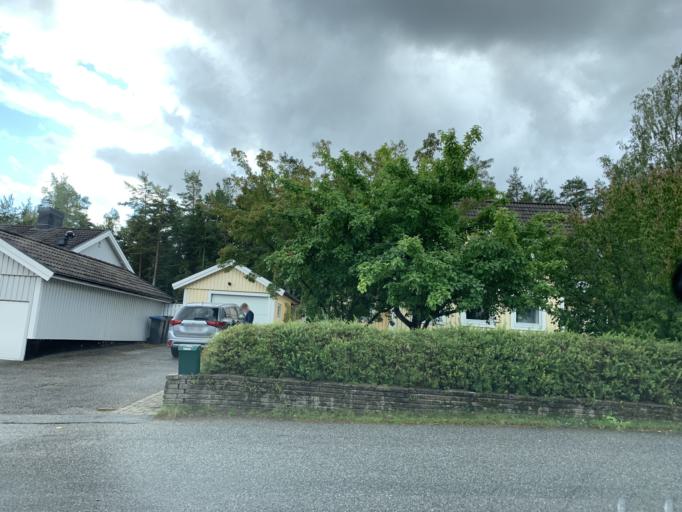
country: SE
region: Stockholm
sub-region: Taby Kommun
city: Taby
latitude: 59.4394
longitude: 18.0140
